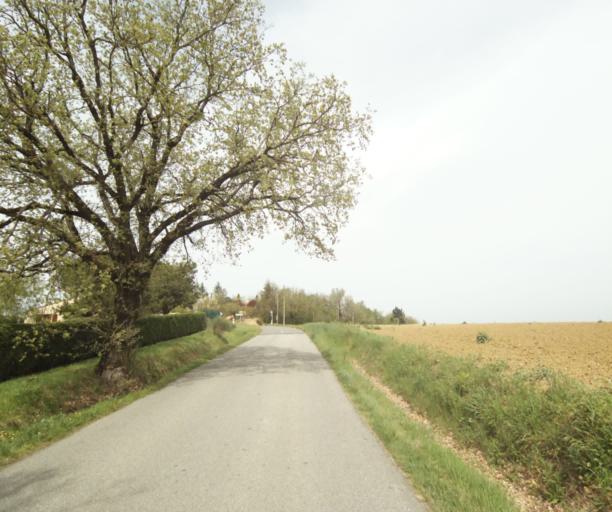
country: FR
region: Midi-Pyrenees
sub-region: Departement de la Haute-Garonne
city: Pompertuzat
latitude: 43.4885
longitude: 1.4999
